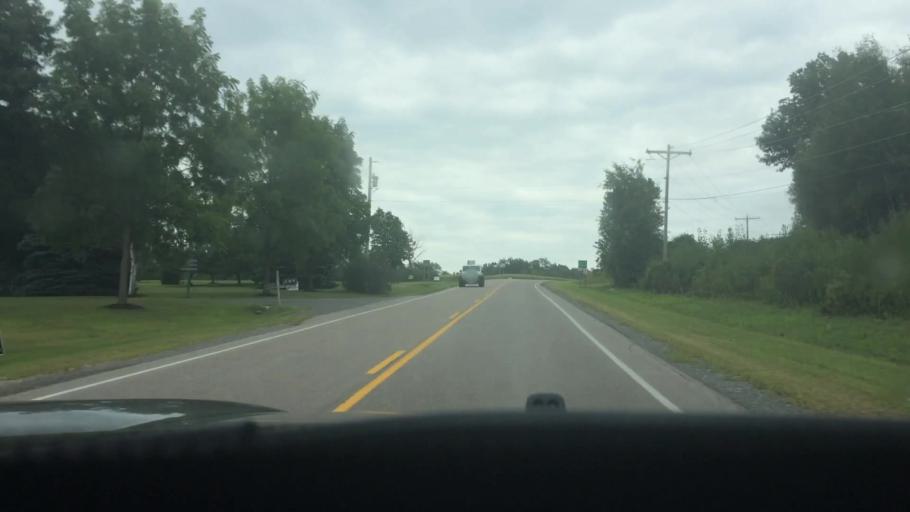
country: US
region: New York
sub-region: St. Lawrence County
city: Canton
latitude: 44.5422
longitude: -75.0923
